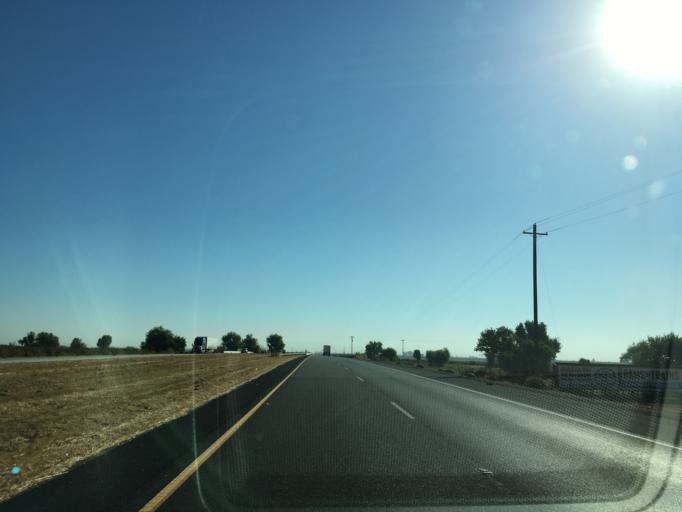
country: US
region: California
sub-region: Madera County
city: Chowchilla
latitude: 37.0832
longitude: -120.3634
